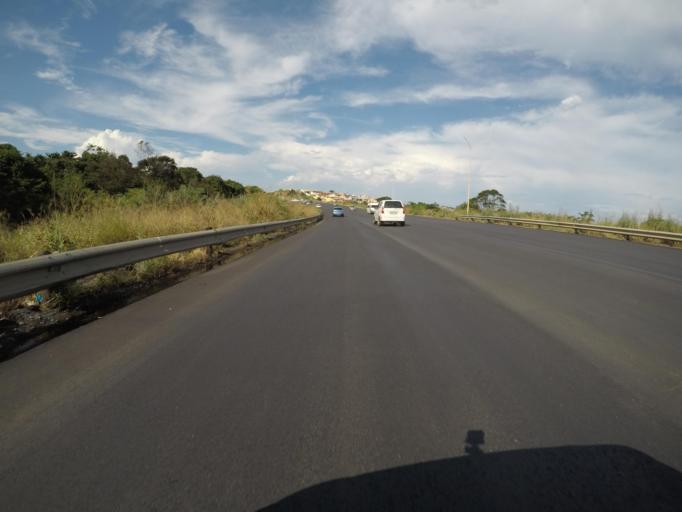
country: ZA
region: Eastern Cape
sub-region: Buffalo City Metropolitan Municipality
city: East London
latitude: -33.0113
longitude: 27.8566
